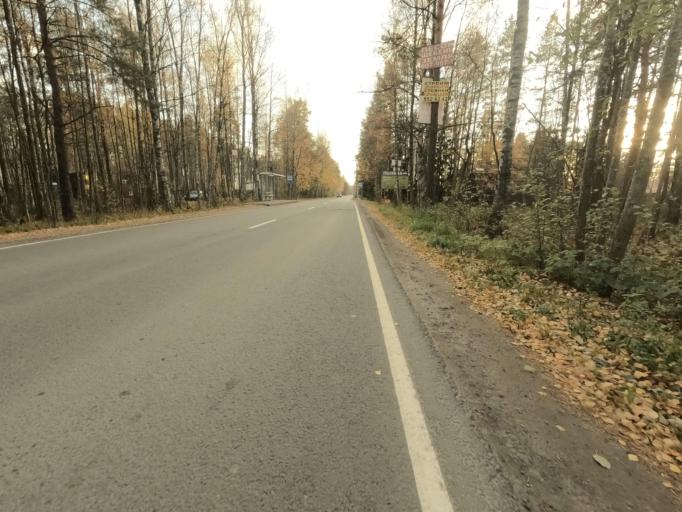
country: RU
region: St.-Petersburg
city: Beloostrov
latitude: 60.1648
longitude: 30.0089
